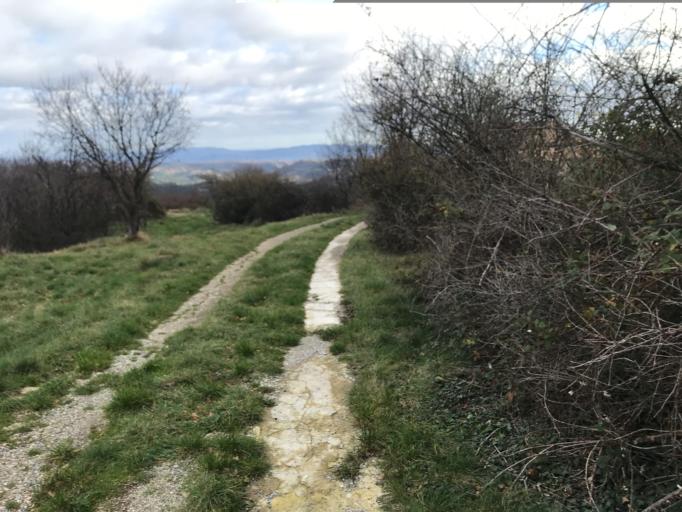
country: FR
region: Rhone-Alpes
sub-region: Departement de l'Ardeche
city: Les Vans
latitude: 44.4212
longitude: 4.0743
